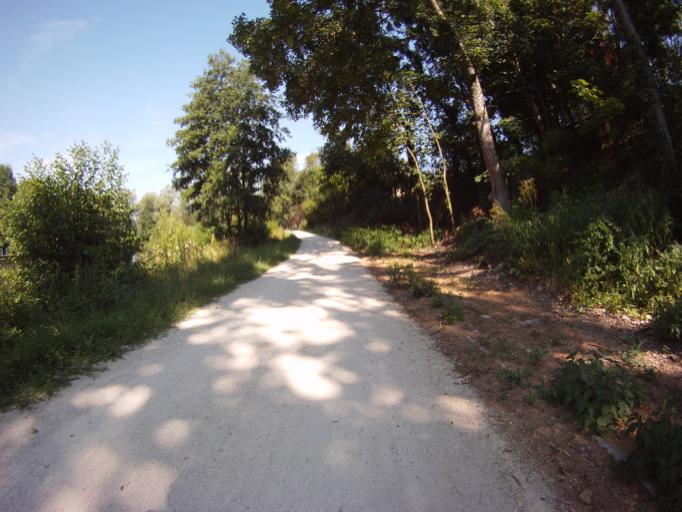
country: FR
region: Lorraine
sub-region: Departement de Meurthe-et-Moselle
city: Liverdun
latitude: 48.7565
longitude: 6.0623
